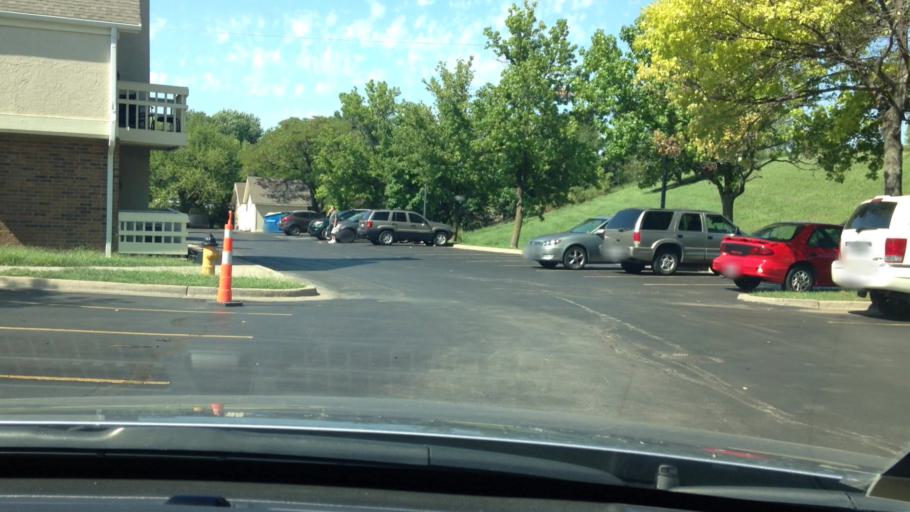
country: US
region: Kansas
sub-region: Johnson County
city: Overland Park
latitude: 38.9296
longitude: -94.6586
